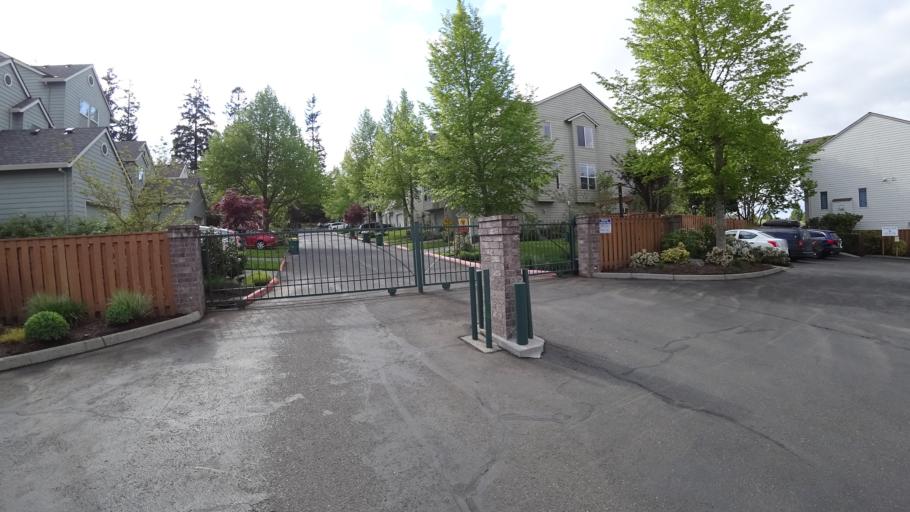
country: US
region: Oregon
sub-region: Washington County
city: Beaverton
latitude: 45.4523
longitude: -122.8365
